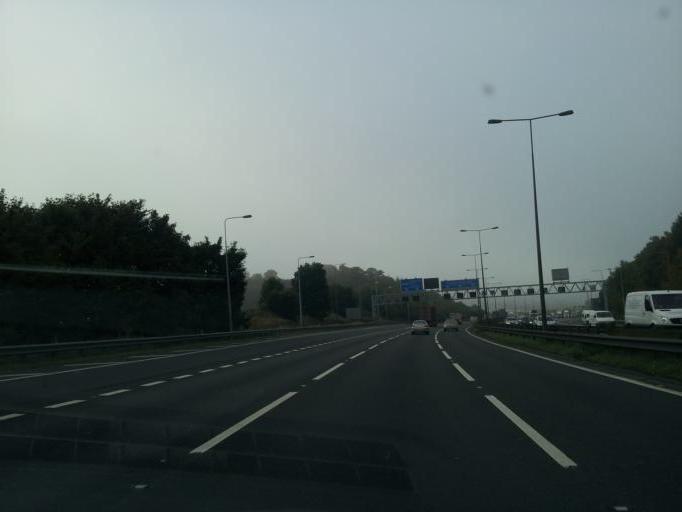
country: GB
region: England
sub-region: Calderdale
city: Brighouse
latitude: 53.6998
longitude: -1.7450
